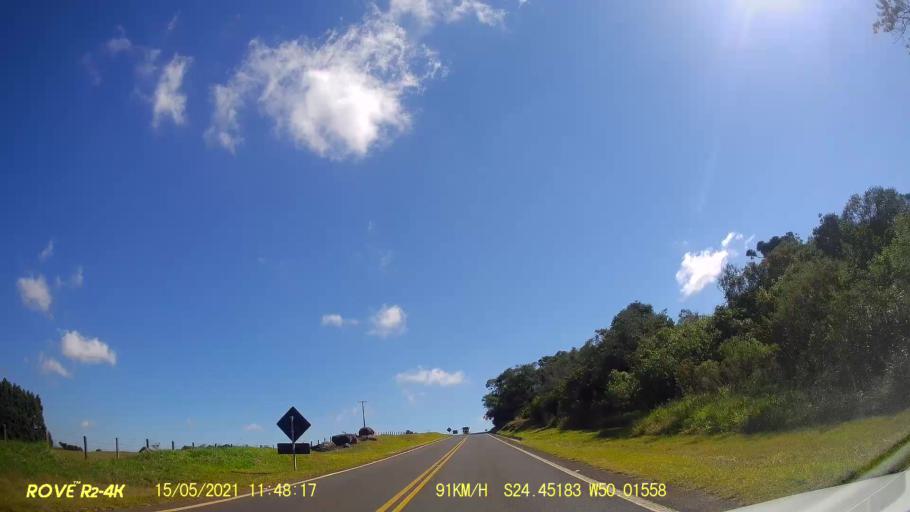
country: BR
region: Parana
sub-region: Pirai Do Sul
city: Pirai do Sul
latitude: -24.4520
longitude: -50.0153
